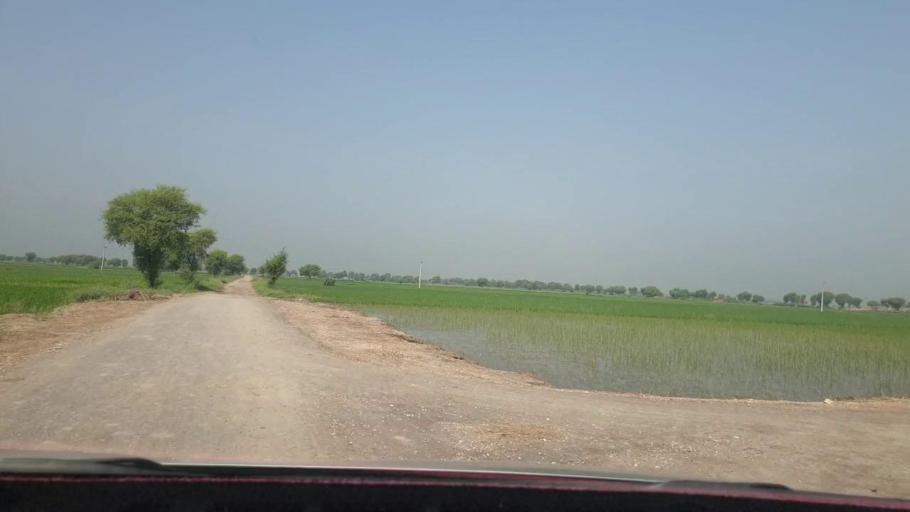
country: PK
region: Sindh
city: Warah
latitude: 27.4310
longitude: 67.8560
